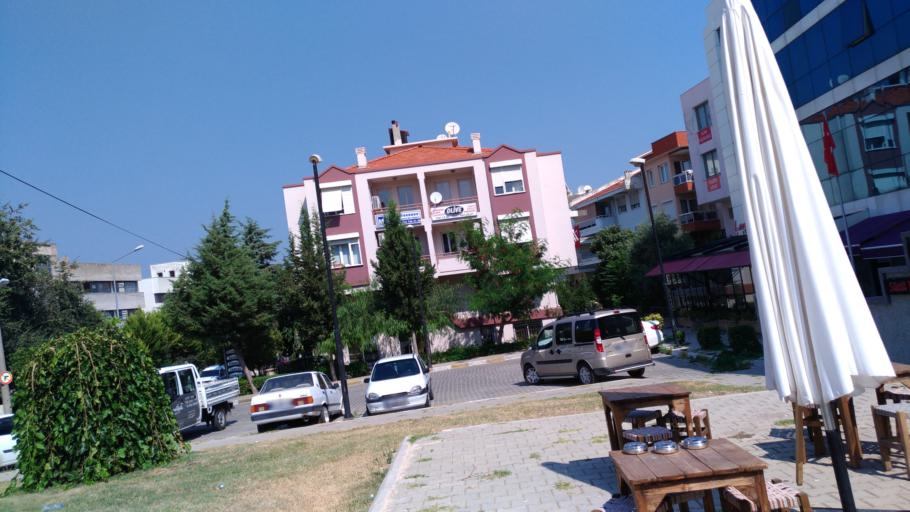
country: TR
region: Izmir
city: Urla
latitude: 38.3248
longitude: 26.7679
